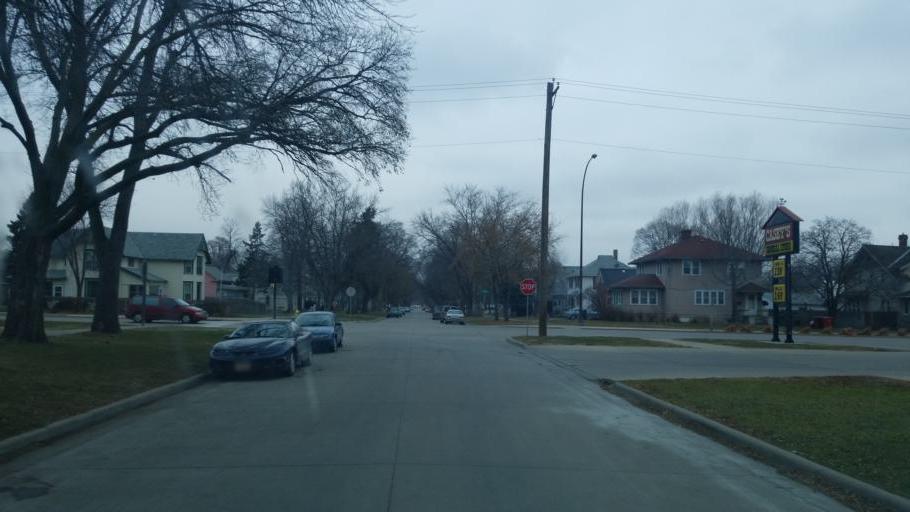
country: US
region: South Dakota
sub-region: Yankton County
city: Yankton
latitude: 42.8708
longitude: -97.4002
